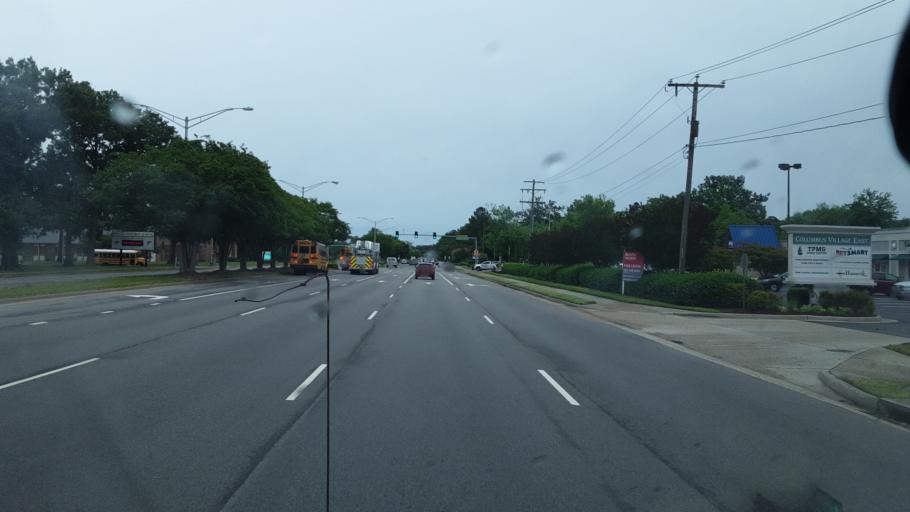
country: US
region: Virginia
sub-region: City of Chesapeake
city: Chesapeake
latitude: 36.8433
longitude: -76.1281
